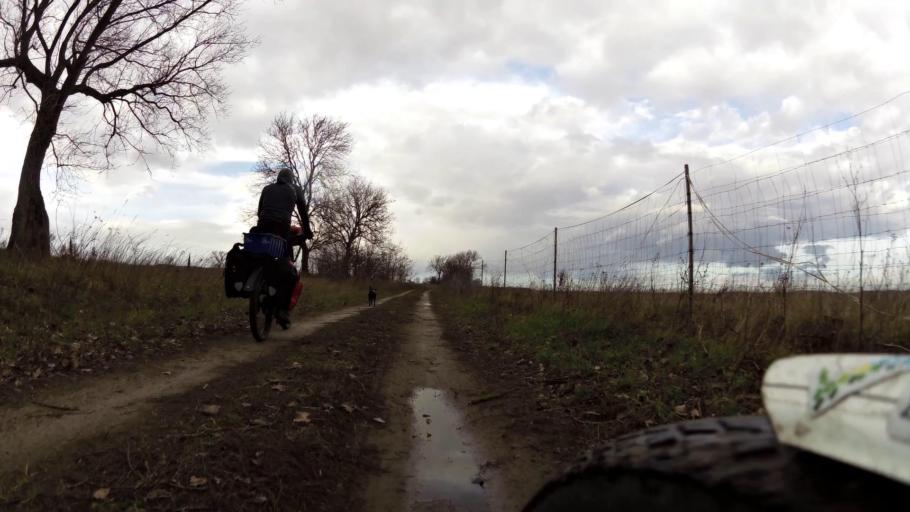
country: PL
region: West Pomeranian Voivodeship
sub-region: Powiat kamienski
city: Wolin
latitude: 53.8760
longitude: 14.7103
